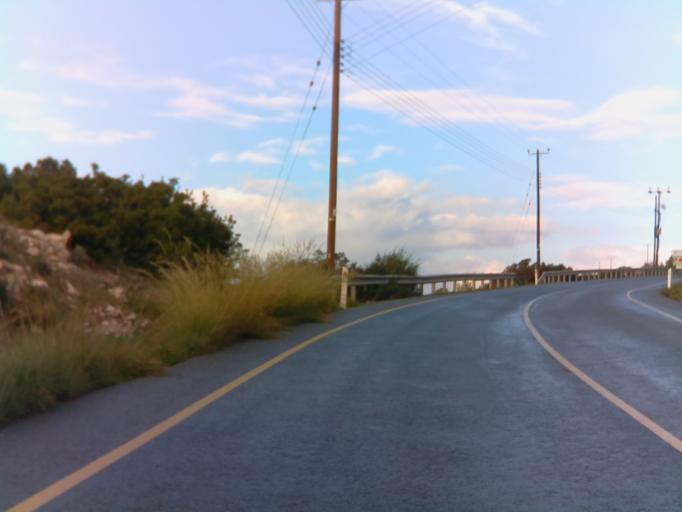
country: CY
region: Pafos
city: Pegeia
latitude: 34.8880
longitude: 32.3722
